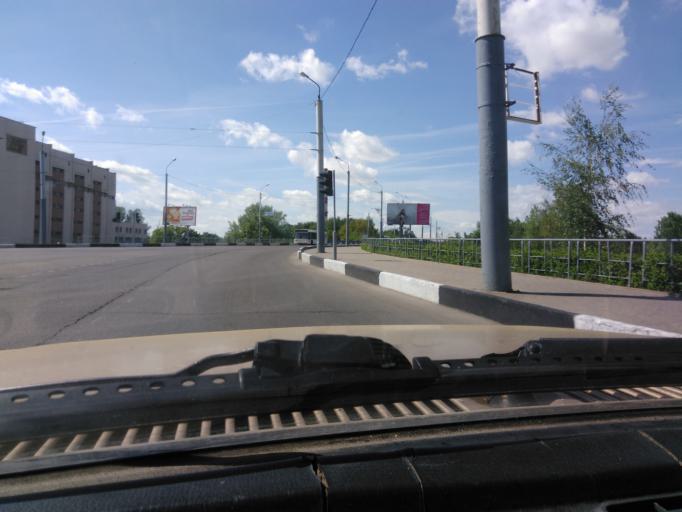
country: BY
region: Mogilev
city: Mahilyow
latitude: 53.9128
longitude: 30.3194
